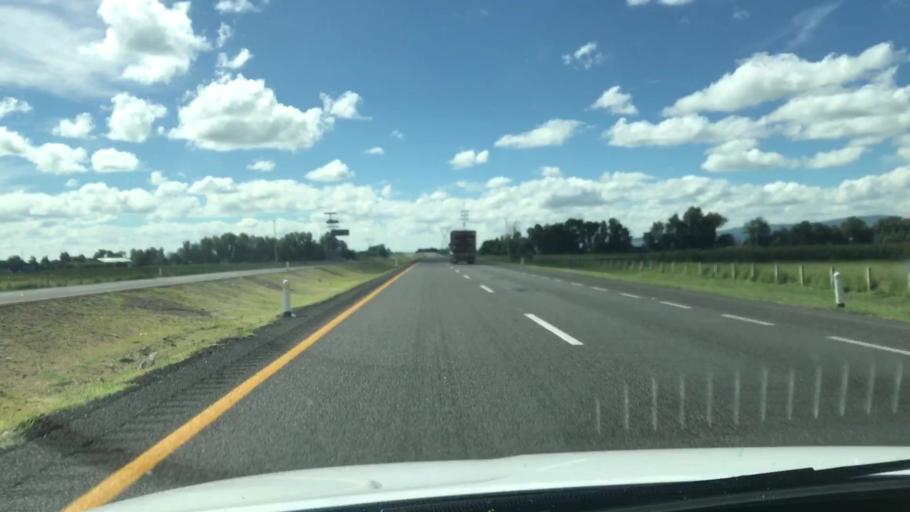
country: MX
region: Guanajuato
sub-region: Silao de la Victoria
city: La Aldea
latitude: 20.8943
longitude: -101.4861
